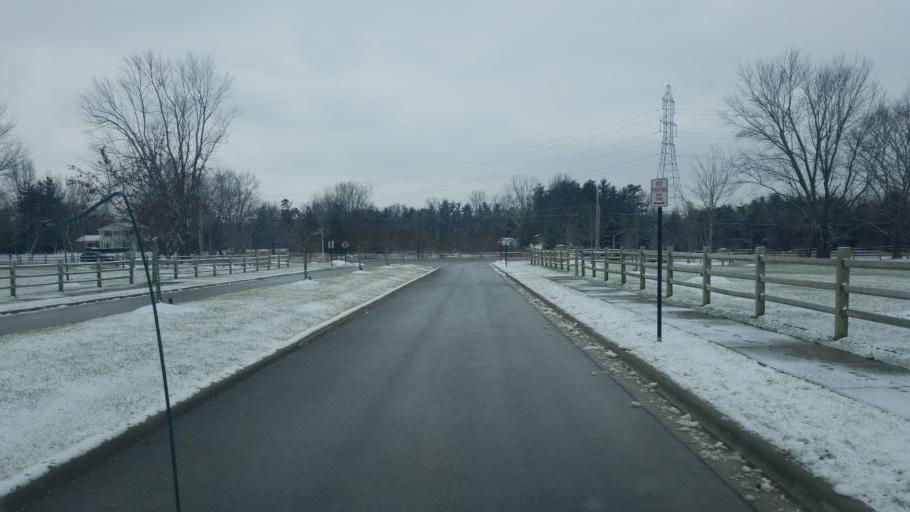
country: US
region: Ohio
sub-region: Franklin County
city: New Albany
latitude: 40.0438
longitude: -82.7917
